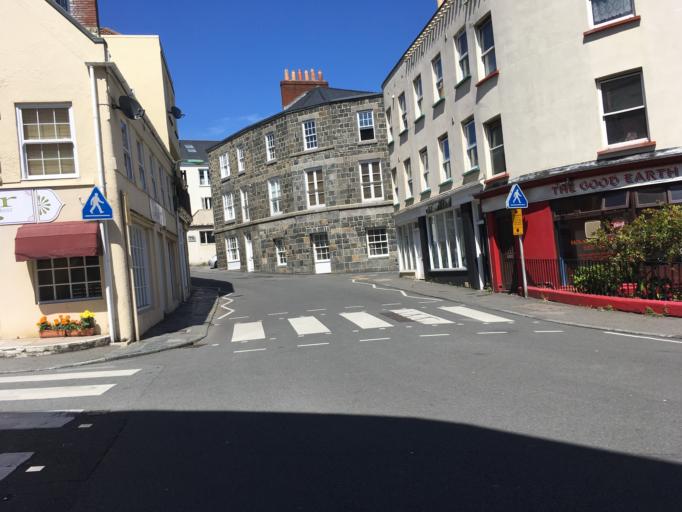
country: GG
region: St Peter Port
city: Saint Peter Port
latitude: 49.4528
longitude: -2.5412
